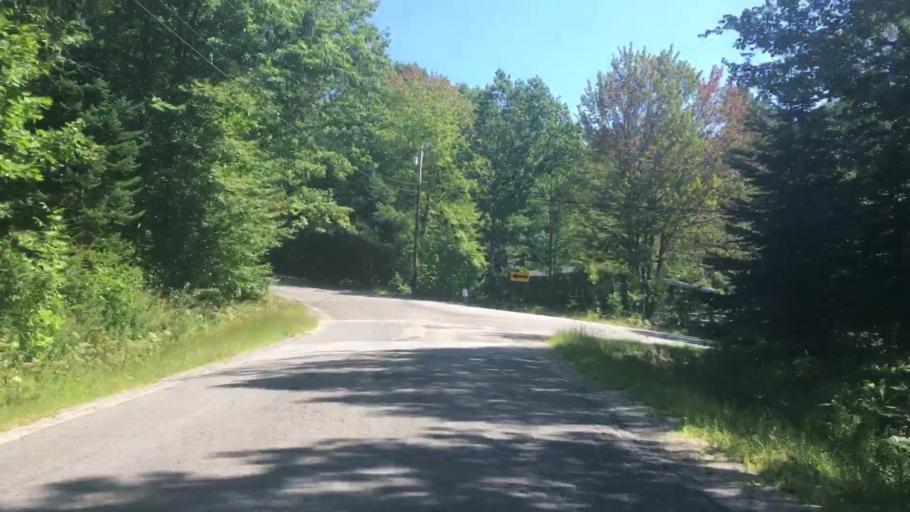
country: US
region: Maine
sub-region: Androscoggin County
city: Sabattus
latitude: 44.1210
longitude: -70.0524
